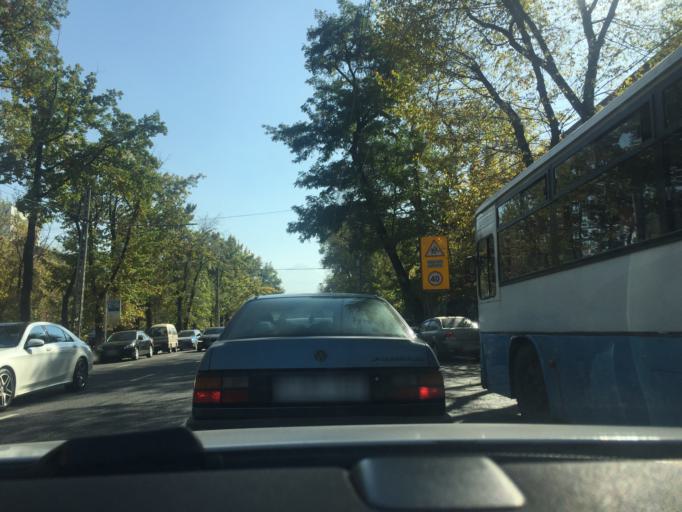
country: KZ
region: Almaty Qalasy
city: Almaty
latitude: 43.2427
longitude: 76.9036
